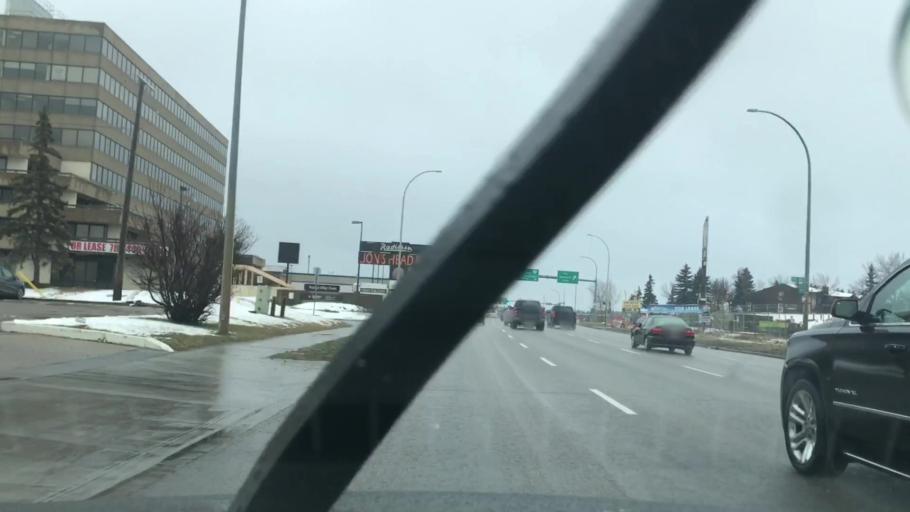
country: CA
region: Alberta
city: Edmonton
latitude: 53.4835
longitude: -113.4949
